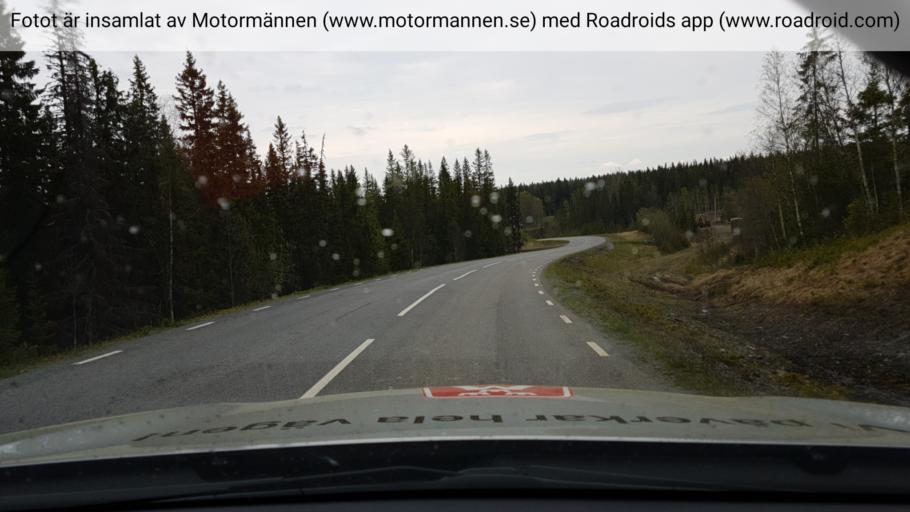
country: SE
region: Jaemtland
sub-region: Are Kommun
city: Are
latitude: 63.5735
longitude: 13.0181
